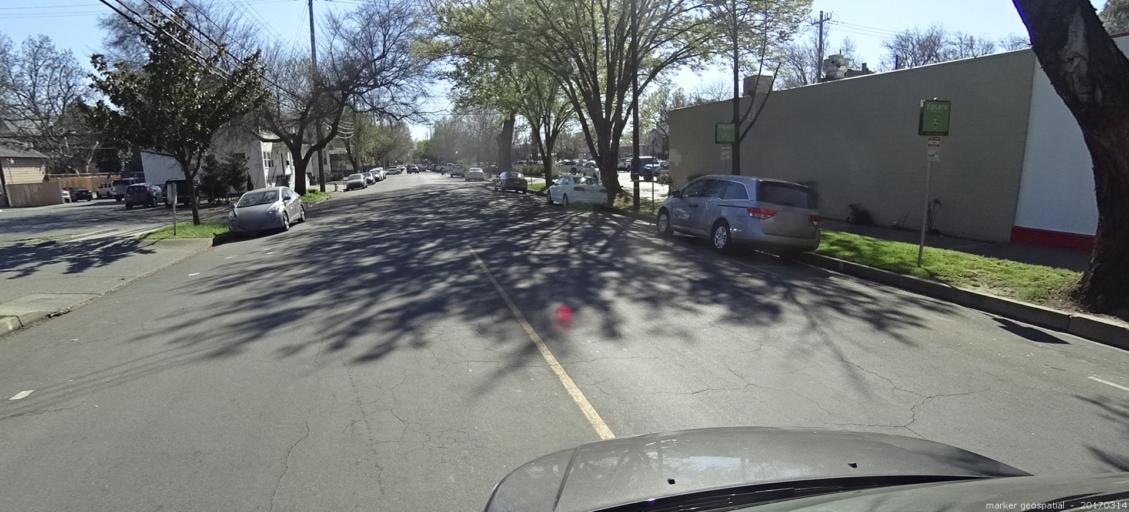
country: US
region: California
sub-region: Sacramento County
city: Sacramento
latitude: 38.5788
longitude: -121.4790
